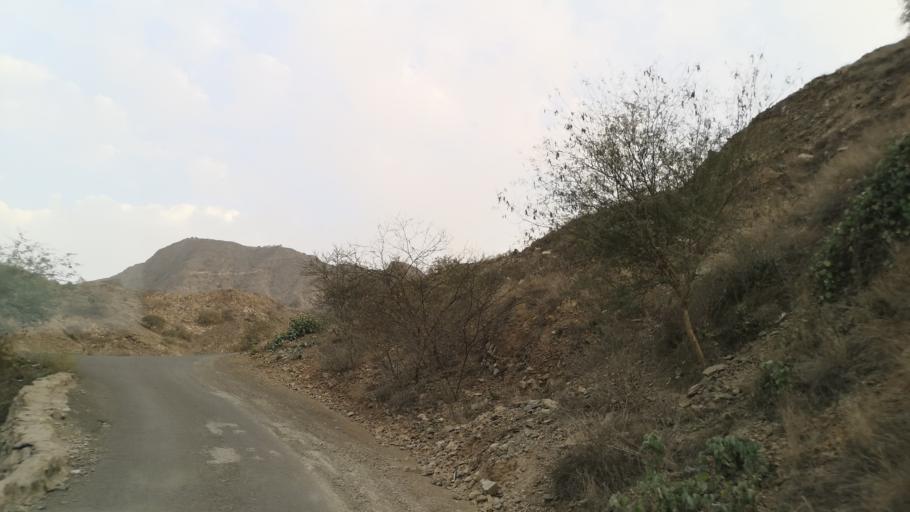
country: YE
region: Sa'dah
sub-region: Monabbih
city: Suq al Khamis
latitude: 17.3272
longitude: 43.1456
